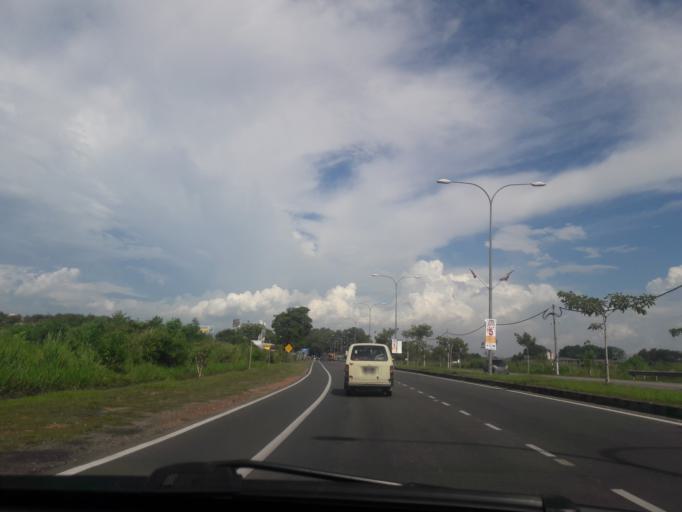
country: MY
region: Kedah
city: Sungai Petani
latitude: 5.6160
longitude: 100.4687
